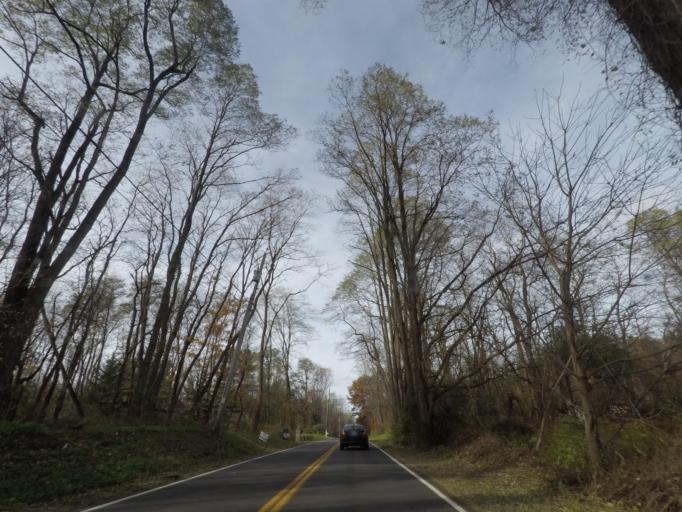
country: US
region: New York
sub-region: Albany County
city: Westmere
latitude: 42.7336
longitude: -73.9076
